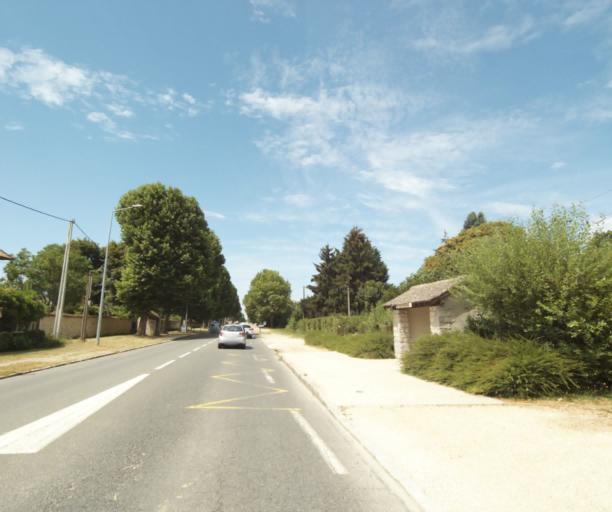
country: FR
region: Ile-de-France
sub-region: Departement de Seine-et-Marne
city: Chailly-en-Biere
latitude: 48.4681
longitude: 2.6056
